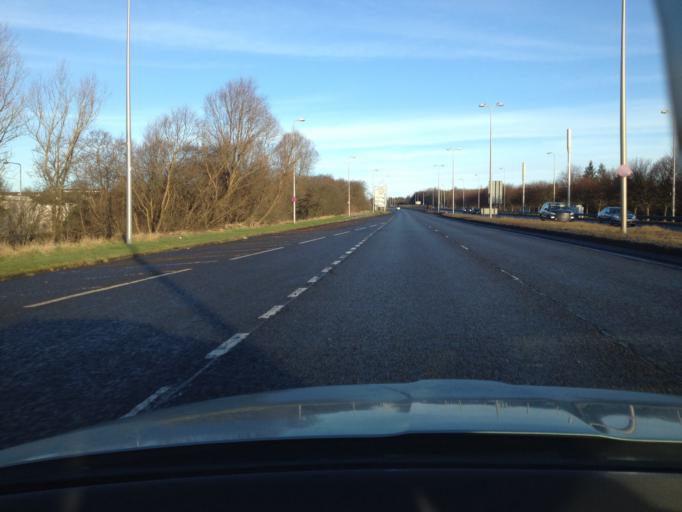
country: GB
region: Scotland
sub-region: West Lothian
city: Livingston
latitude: 55.8920
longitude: -3.5039
